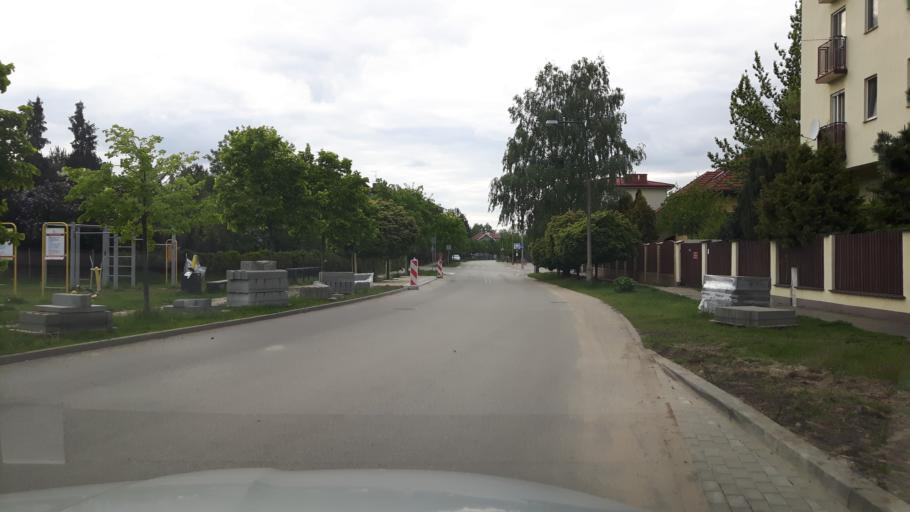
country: PL
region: Masovian Voivodeship
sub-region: Powiat wolominski
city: Zabki
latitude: 52.2804
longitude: 21.0830
